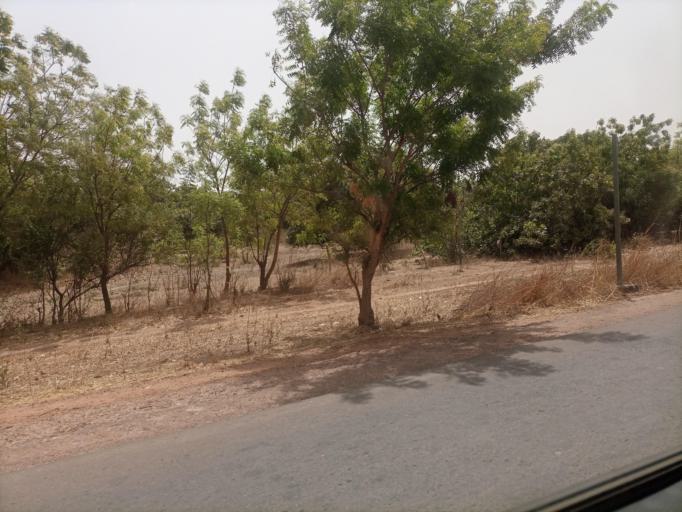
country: SN
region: Fatick
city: Sokone
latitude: 13.7186
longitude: -16.4252
